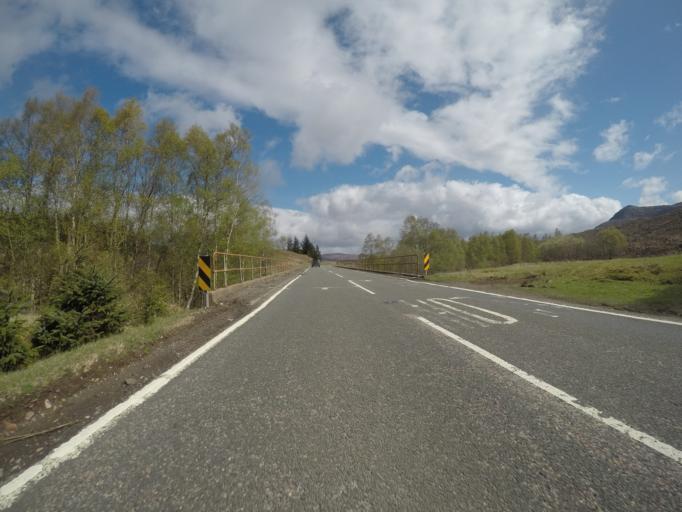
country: GB
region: Scotland
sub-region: Highland
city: Spean Bridge
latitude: 57.1324
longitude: -4.9580
